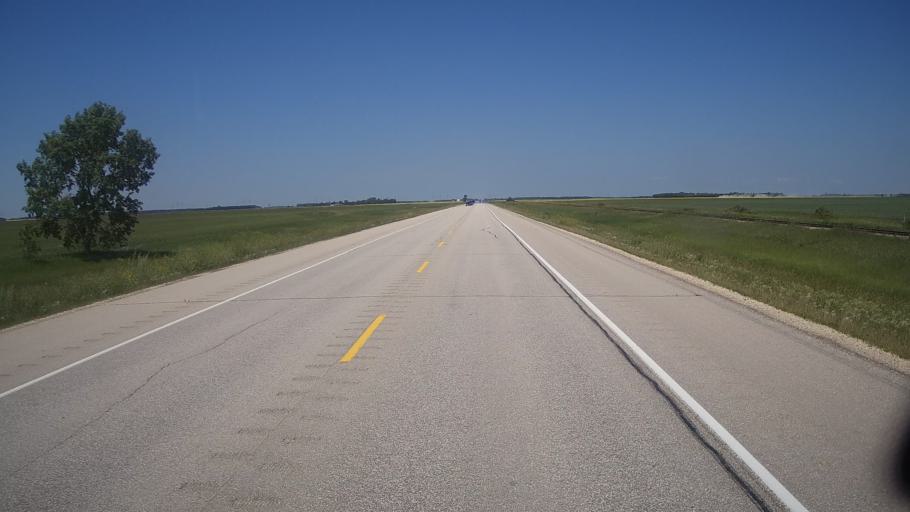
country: CA
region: Manitoba
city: Stonewall
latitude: 50.0209
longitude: -97.3761
